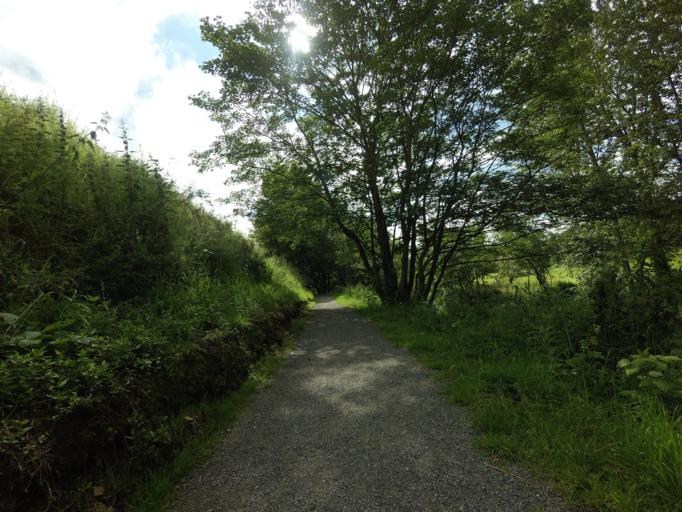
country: GB
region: Scotland
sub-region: Aberdeenshire
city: Turriff
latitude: 57.5382
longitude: -2.4705
